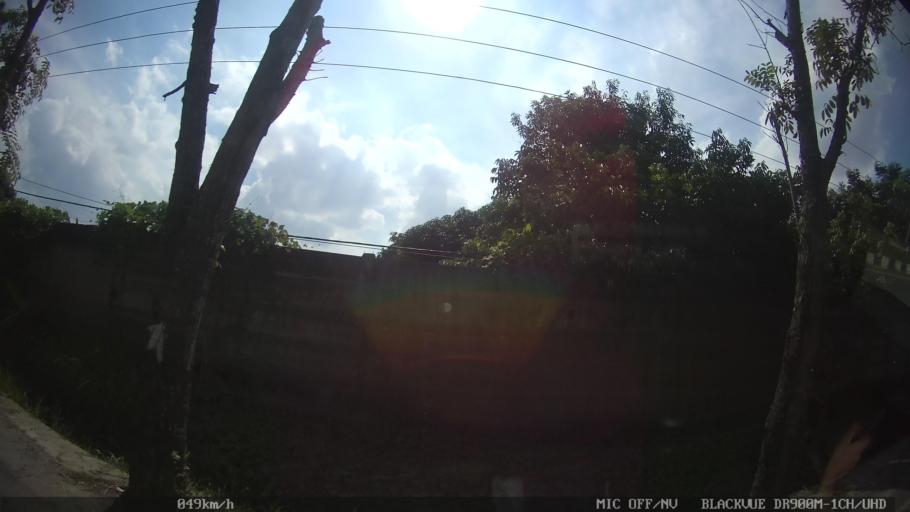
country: ID
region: North Sumatra
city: Binjai
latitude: 3.6338
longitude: 98.5351
